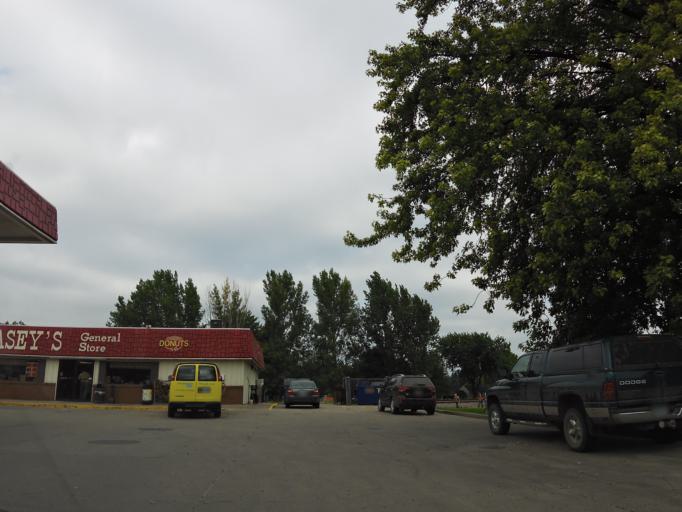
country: US
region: Minnesota
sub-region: Renville County
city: Olivia
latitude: 44.7767
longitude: -94.9859
